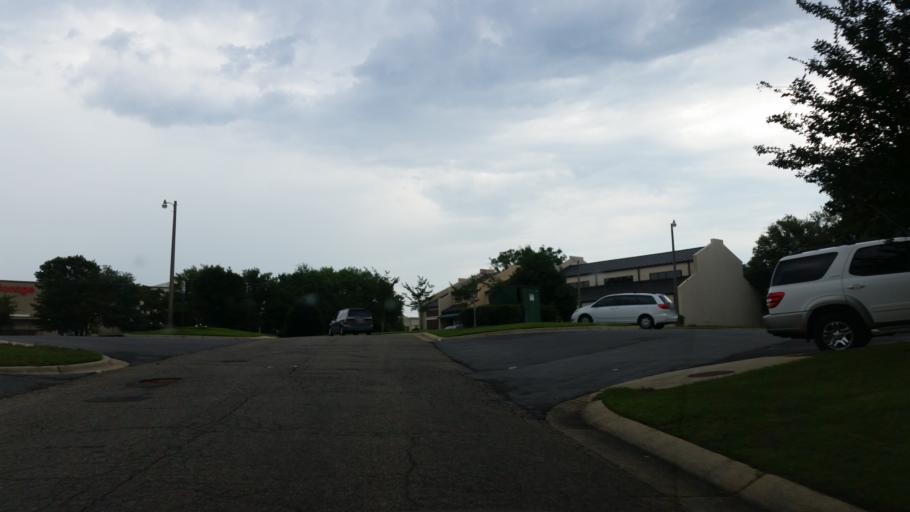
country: US
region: Florida
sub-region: Escambia County
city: Ferry Pass
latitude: 30.4984
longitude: -87.2286
